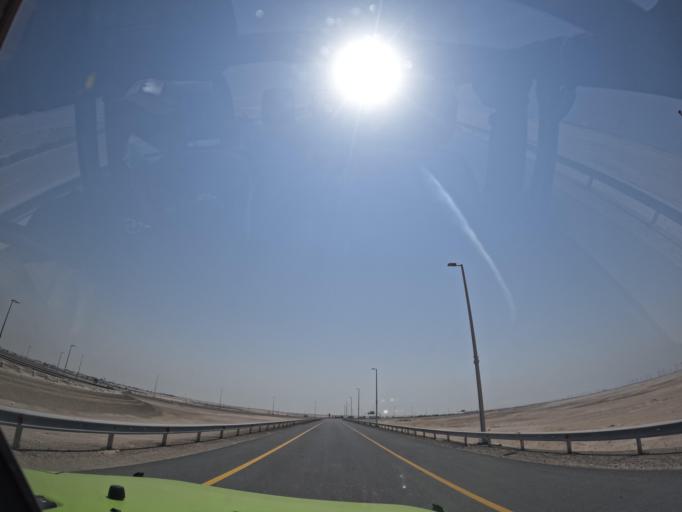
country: AE
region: Abu Dhabi
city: Abu Dhabi
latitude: 24.2468
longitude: 54.4692
